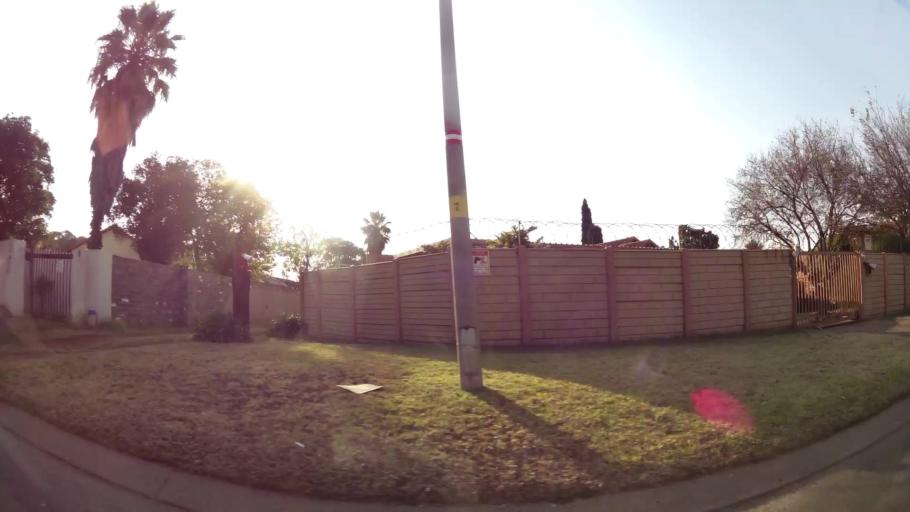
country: ZA
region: Gauteng
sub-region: City of Johannesburg Metropolitan Municipality
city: Modderfontein
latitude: -26.0694
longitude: 28.2141
